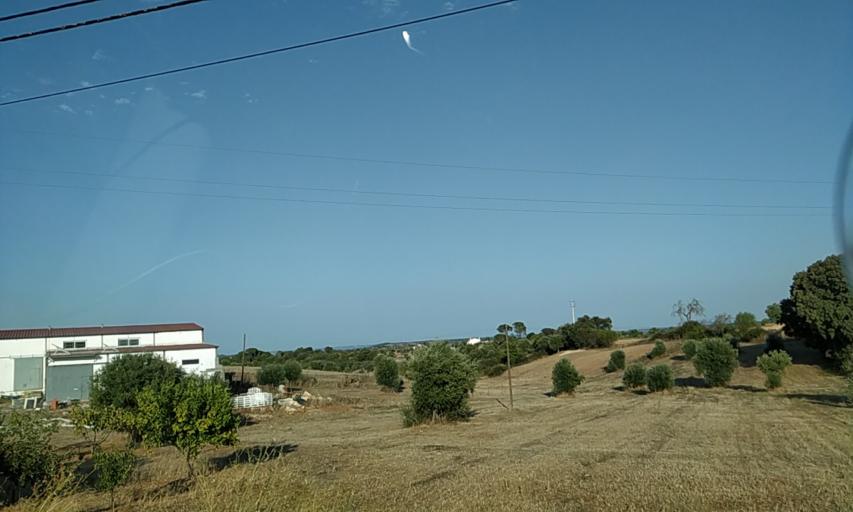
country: PT
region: Santarem
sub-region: Alcanena
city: Alcanena
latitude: 39.3519
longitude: -8.6645
